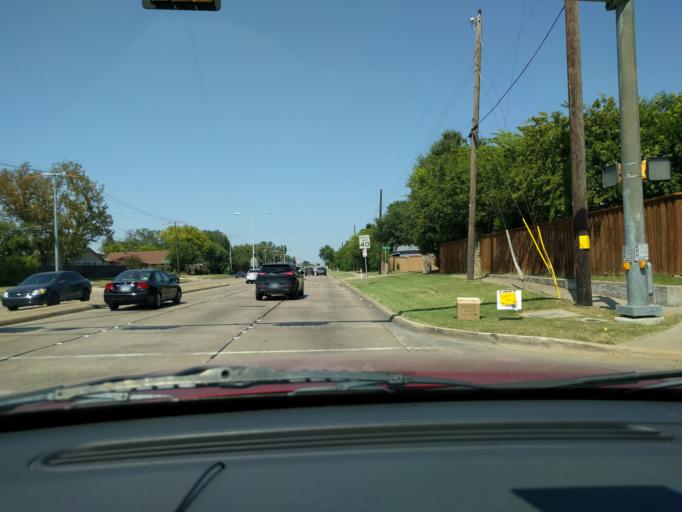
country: US
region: Texas
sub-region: Dallas County
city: Richardson
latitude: 32.9240
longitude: -96.7001
